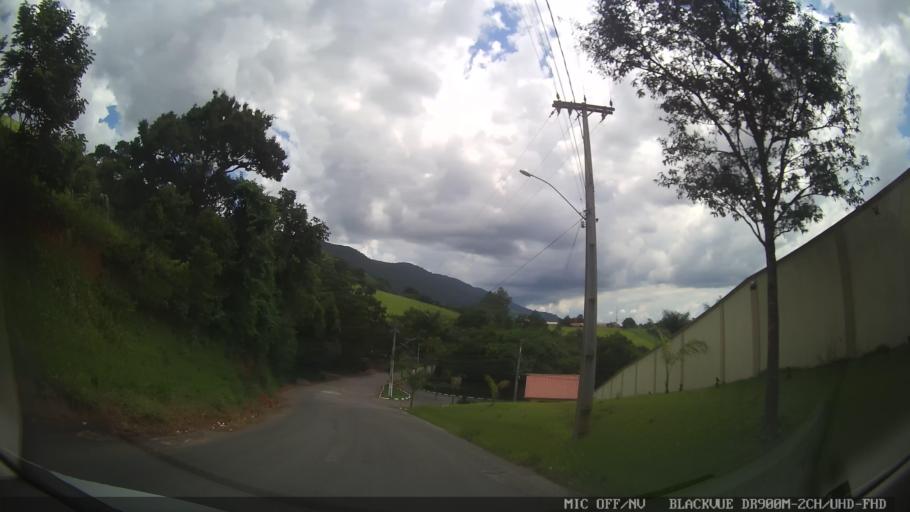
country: BR
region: Minas Gerais
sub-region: Extrema
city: Extrema
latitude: -22.8452
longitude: -46.2975
